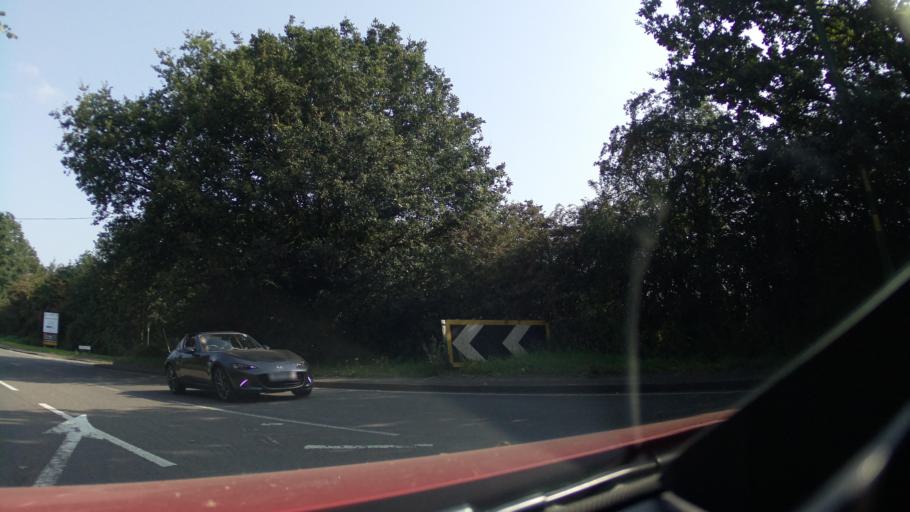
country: GB
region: England
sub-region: Walsall
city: Streetly
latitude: 52.6066
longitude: -1.8874
